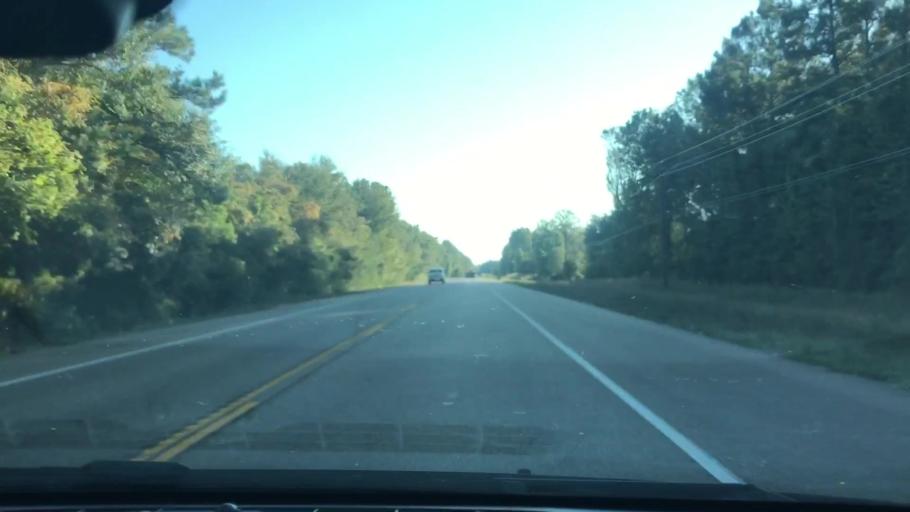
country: US
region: Louisiana
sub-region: Saint Tammany Parish
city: Abita Springs
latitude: 30.5570
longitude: -89.8722
